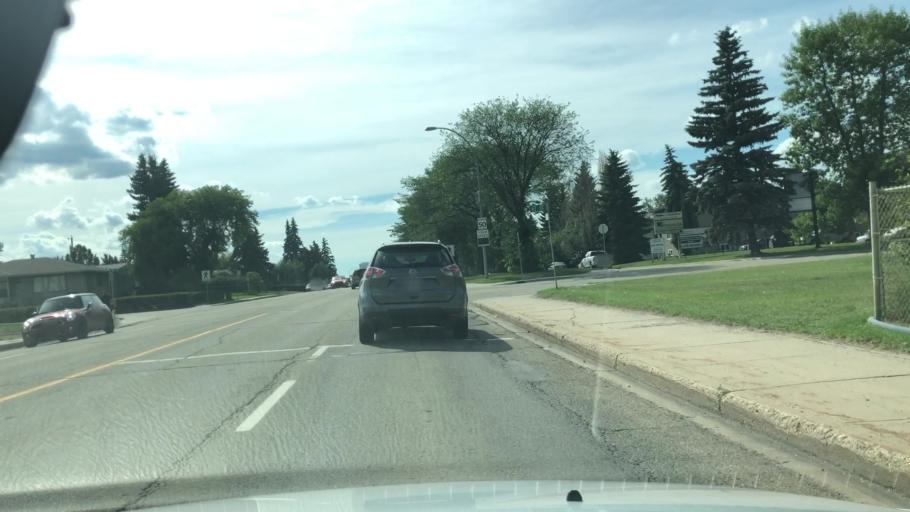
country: CA
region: Alberta
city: Edmonton
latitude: 53.5405
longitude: -113.4306
